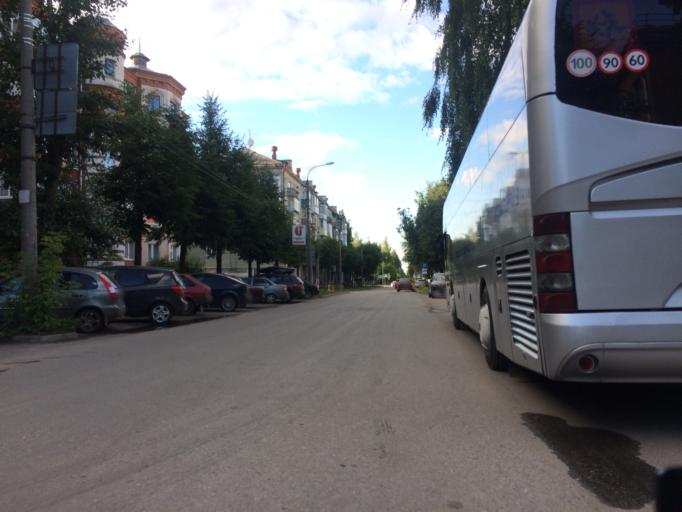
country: RU
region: Mariy-El
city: Yoshkar-Ola
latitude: 56.6366
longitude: 47.8813
